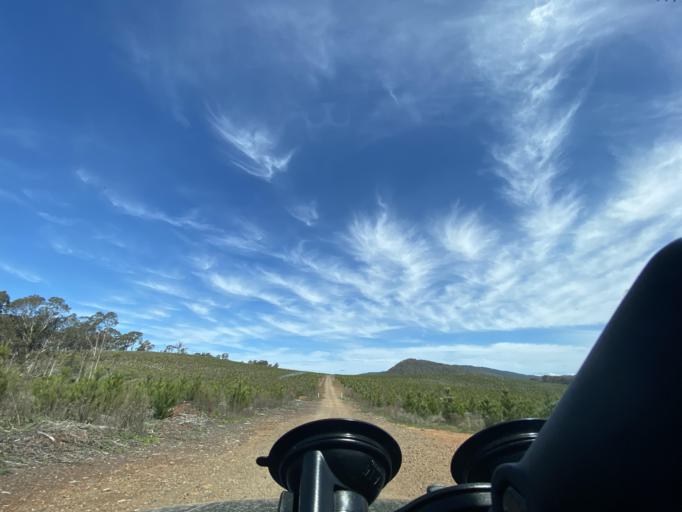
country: AU
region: Victoria
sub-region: Mansfield
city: Mansfield
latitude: -36.8195
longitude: 146.1024
